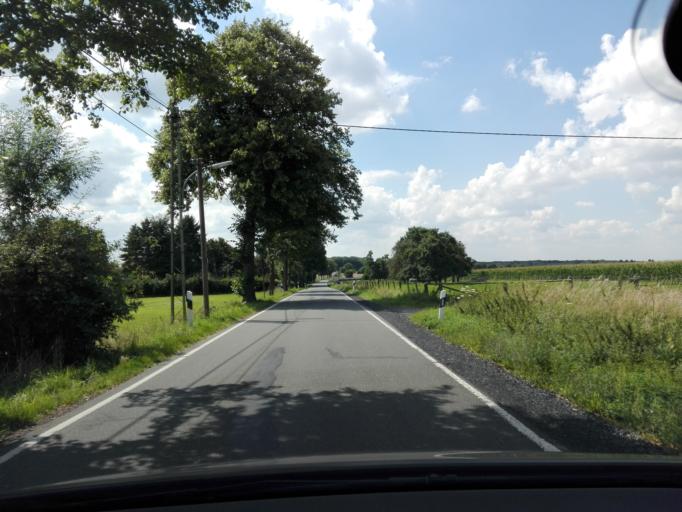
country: DE
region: North Rhine-Westphalia
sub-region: Regierungsbezirk Arnsberg
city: Unna
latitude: 51.4950
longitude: 7.6839
